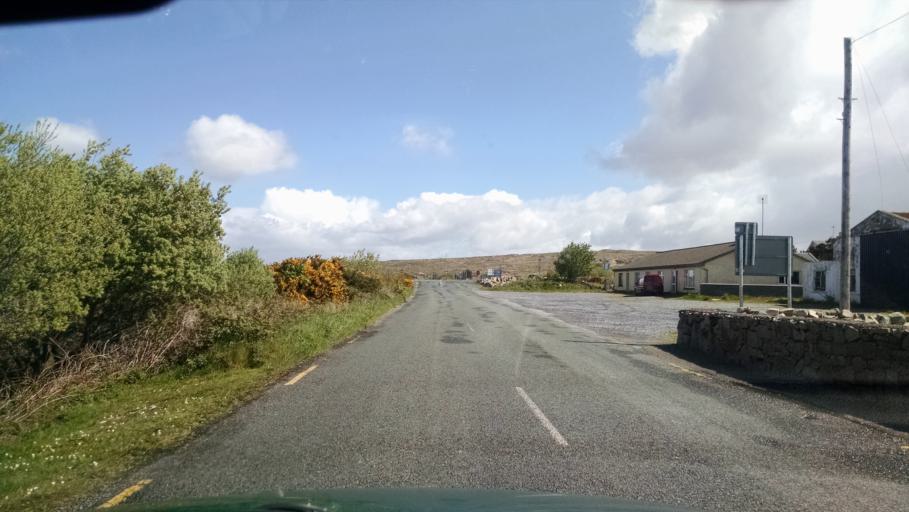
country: IE
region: Connaught
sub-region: County Galway
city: Oughterard
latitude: 53.2763
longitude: -9.5323
